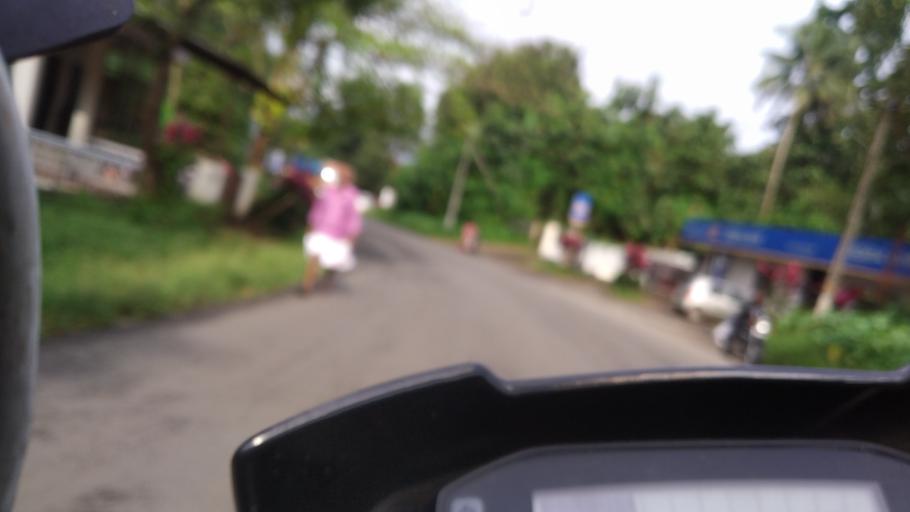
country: IN
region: Kerala
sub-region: Ernakulam
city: Kotamangalam
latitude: 10.0495
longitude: 76.7188
